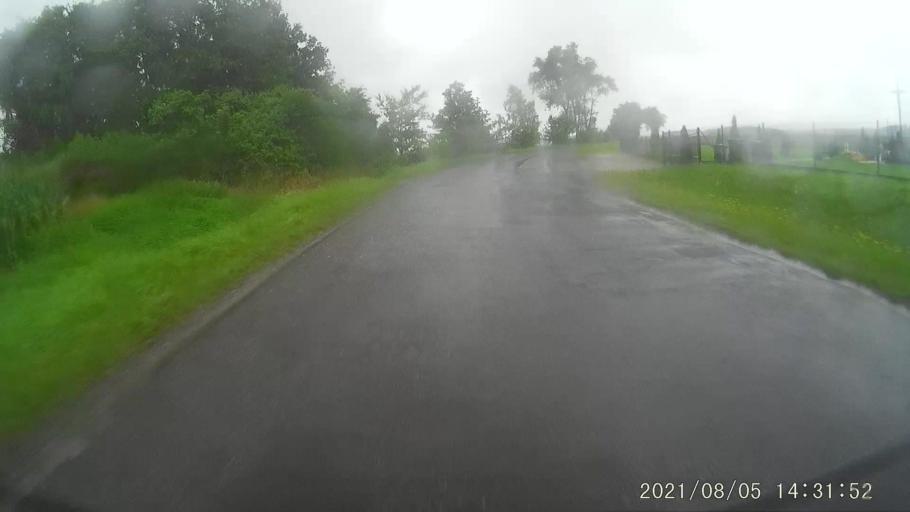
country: PL
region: Opole Voivodeship
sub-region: Powiat nyski
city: Korfantow
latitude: 50.4711
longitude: 17.5529
